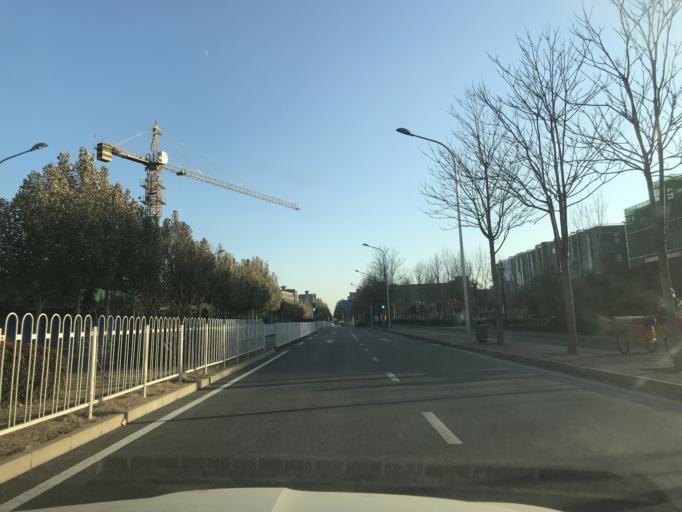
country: CN
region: Beijing
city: Xibeiwang
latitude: 40.0705
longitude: 116.2463
